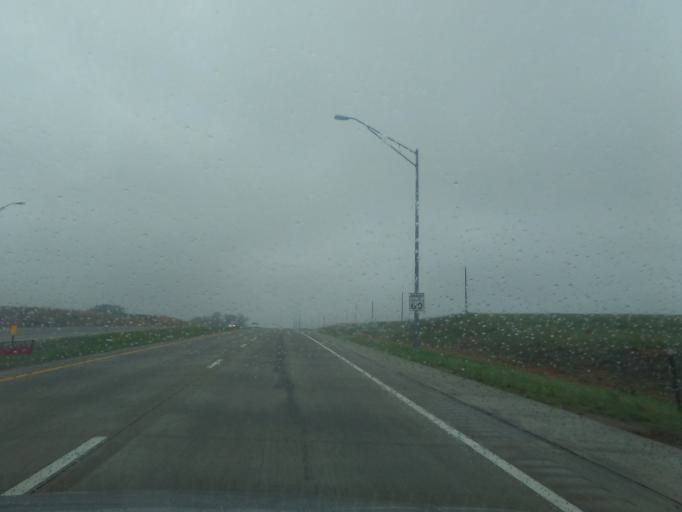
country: US
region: Nebraska
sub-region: Madison County
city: Norfolk
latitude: 42.0659
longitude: -97.3449
